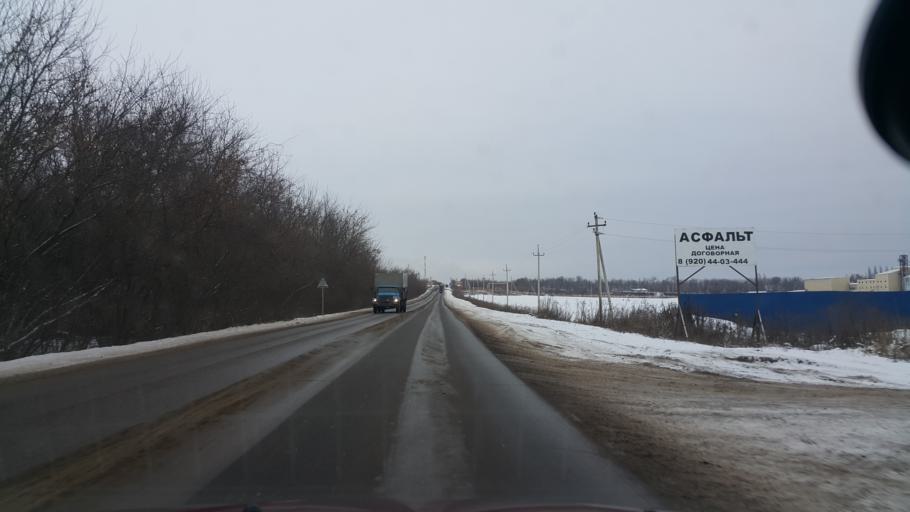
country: RU
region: Tambov
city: Pokrovo-Prigorodnoye
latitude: 52.6561
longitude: 41.4051
